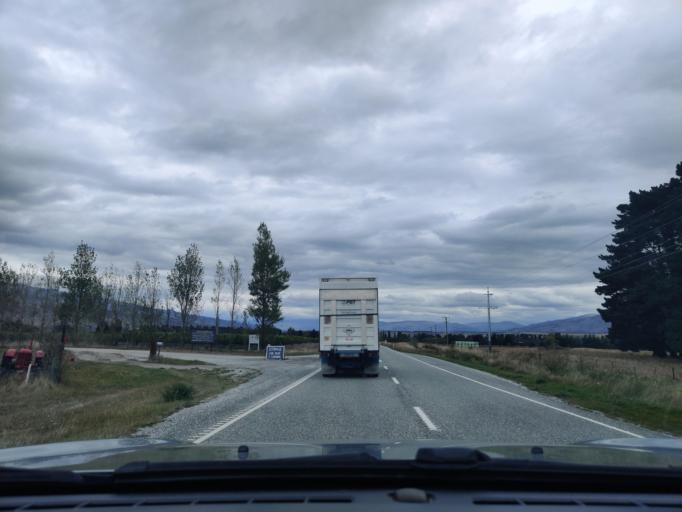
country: NZ
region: Otago
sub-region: Queenstown-Lakes District
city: Wanaka
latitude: -44.9321
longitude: 169.2672
